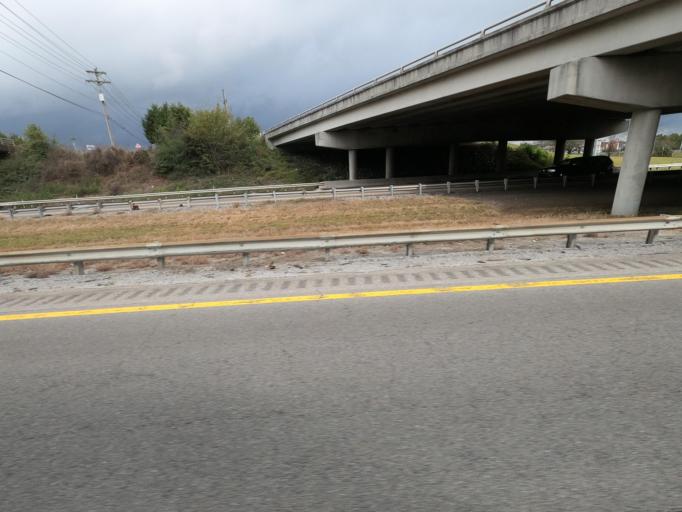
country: US
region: Tennessee
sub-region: Dickson County
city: Burns
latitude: 36.0195
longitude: -87.3367
